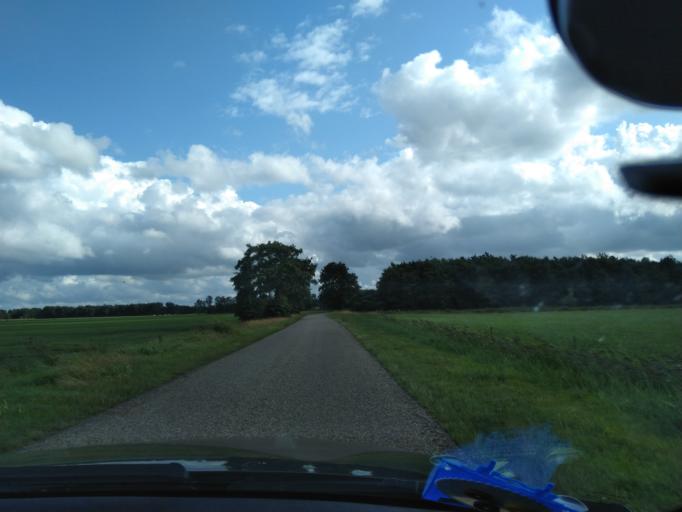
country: NL
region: Drenthe
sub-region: Gemeente Tynaarlo
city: Vries
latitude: 53.0652
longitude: 6.5461
